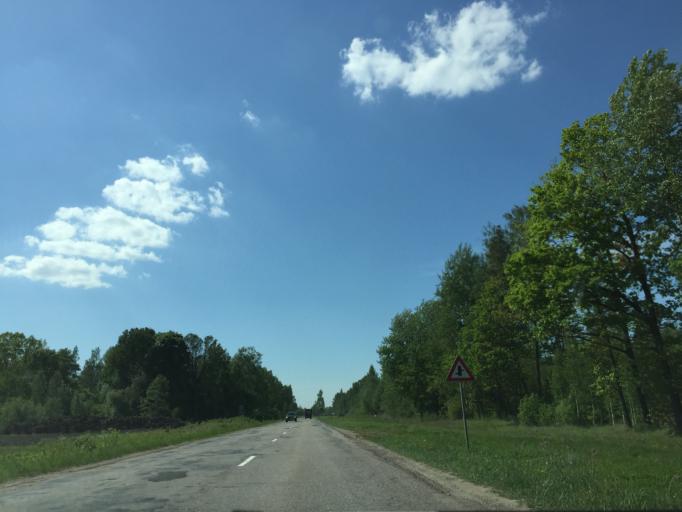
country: LV
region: Ozolnieku
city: Ozolnieki
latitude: 56.6434
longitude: 23.8403
